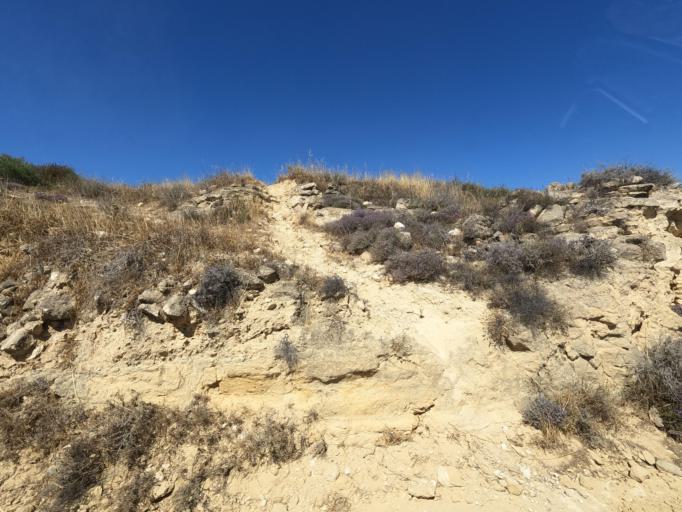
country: CY
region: Larnaka
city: Voroklini
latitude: 34.9921
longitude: 33.6519
